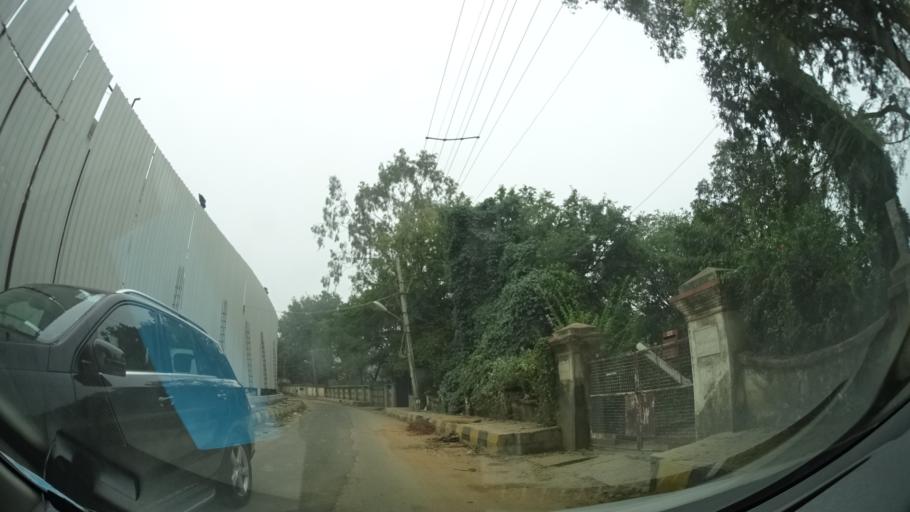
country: IN
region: Karnataka
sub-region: Bangalore Rural
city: Hoskote
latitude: 12.9719
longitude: 77.7468
